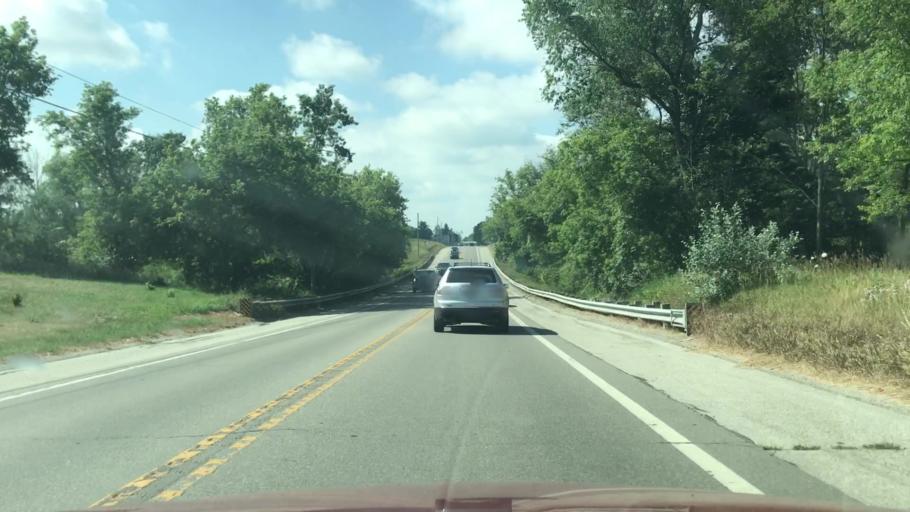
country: US
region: Michigan
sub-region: Kent County
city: Kent City
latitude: 43.3016
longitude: -85.8106
